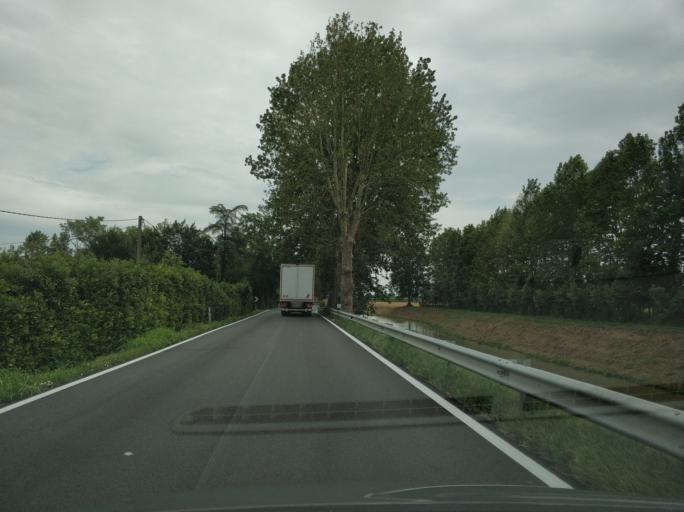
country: IT
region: Veneto
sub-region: Provincia di Padova
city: Lozzo Atestino
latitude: 45.2660
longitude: 11.6011
